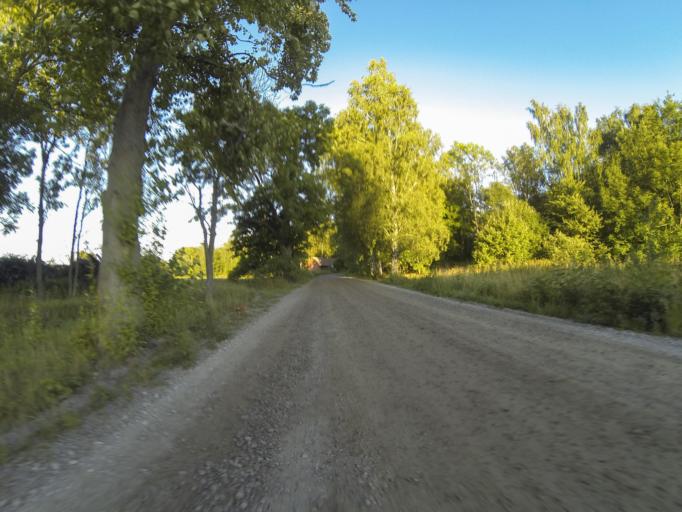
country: SE
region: Vaestmanland
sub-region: Vasteras
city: Vasteras
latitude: 59.5550
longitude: 16.6656
